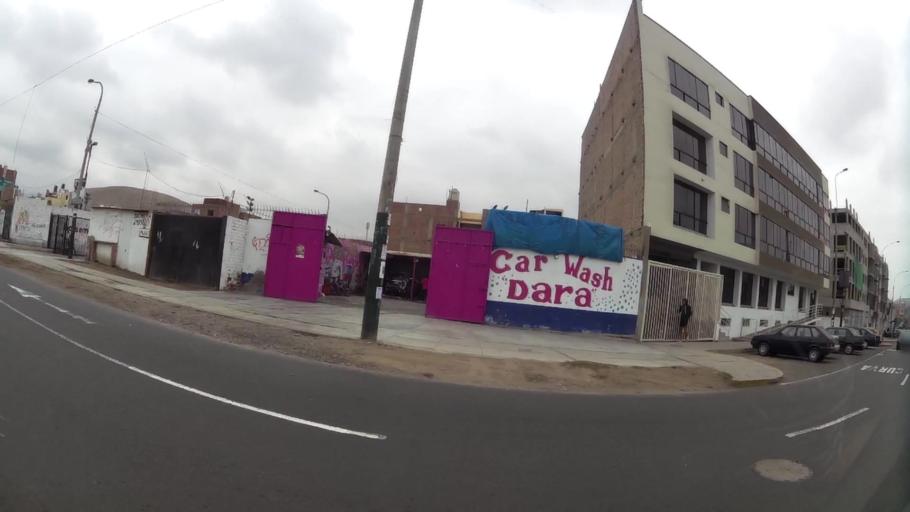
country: PE
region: Lima
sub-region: Lima
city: Surco
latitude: -12.1698
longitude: -76.9921
